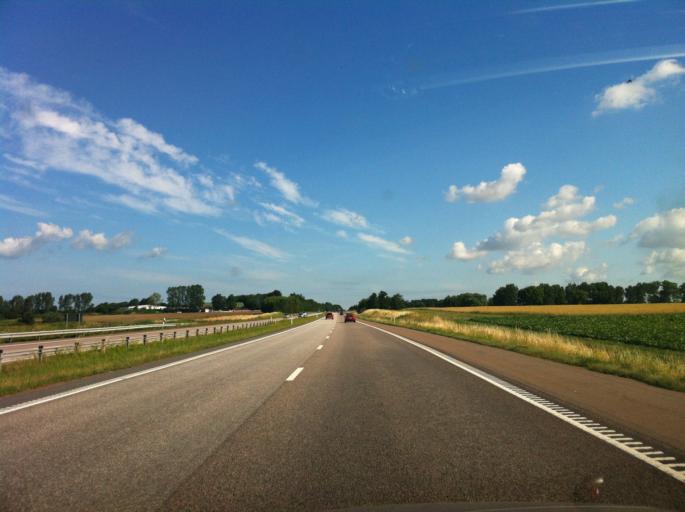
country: SE
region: Skane
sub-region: Angelholms Kommun
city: Strovelstorp
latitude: 56.1487
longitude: 12.8447
